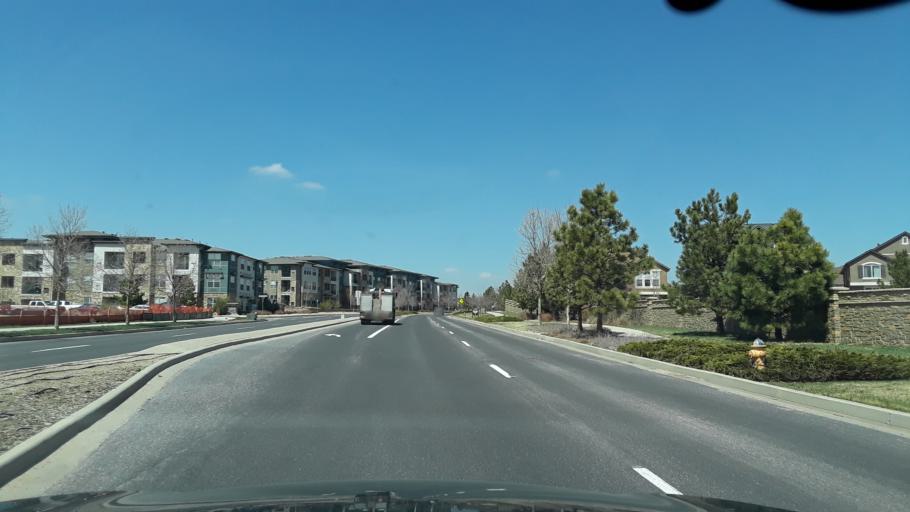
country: US
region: Colorado
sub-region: El Paso County
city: Black Forest
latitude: 38.9733
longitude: -104.7393
